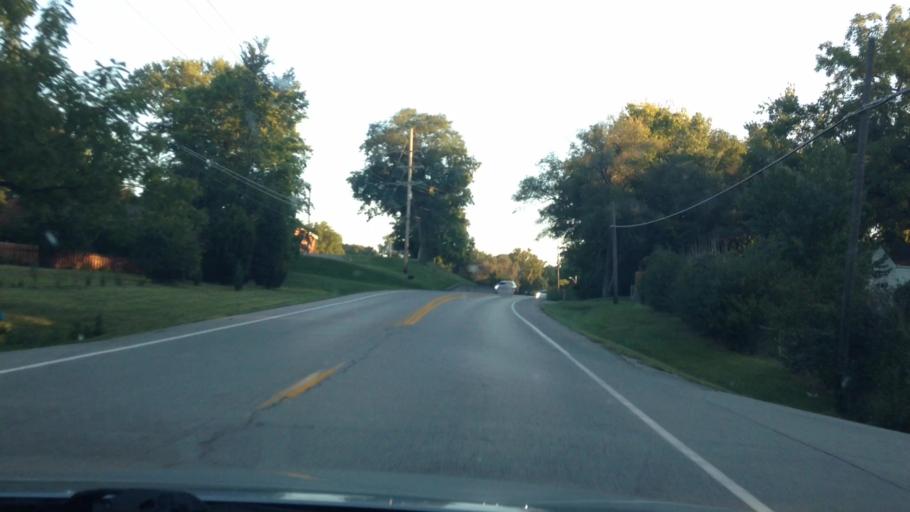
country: US
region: Missouri
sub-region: Platte County
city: Weatherby Lake
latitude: 39.2275
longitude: -94.6590
